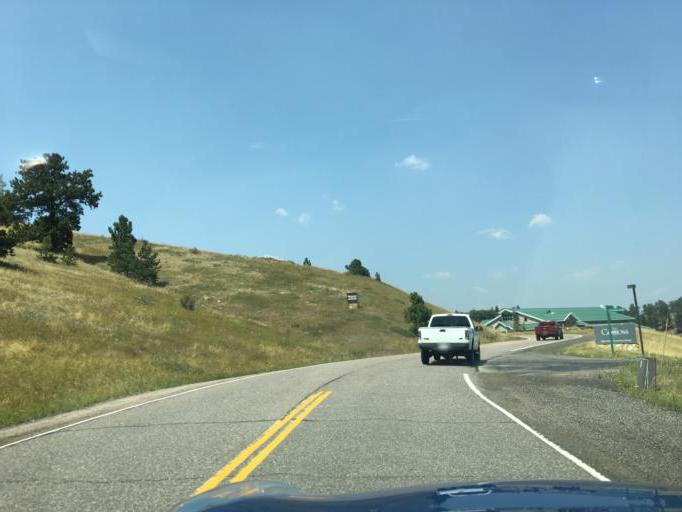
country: US
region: Colorado
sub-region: Jefferson County
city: Genesee
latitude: 39.7049
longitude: -105.2807
